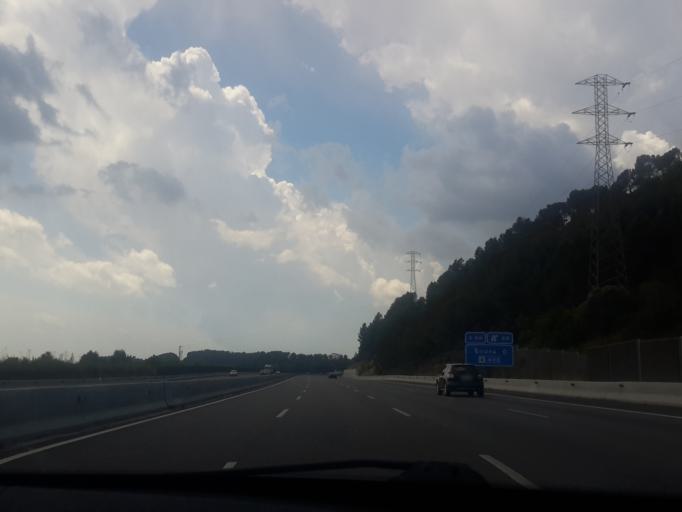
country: ES
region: Catalonia
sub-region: Provincia de Girona
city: Sarria de Ter
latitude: 42.0193
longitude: 2.8150
